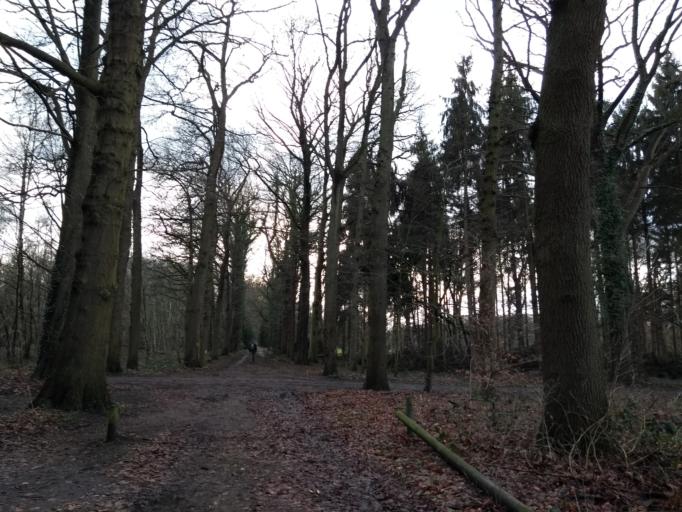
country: NL
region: Overijssel
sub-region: Gemeente Enschede
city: Enschede
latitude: 52.2575
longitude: 6.8755
